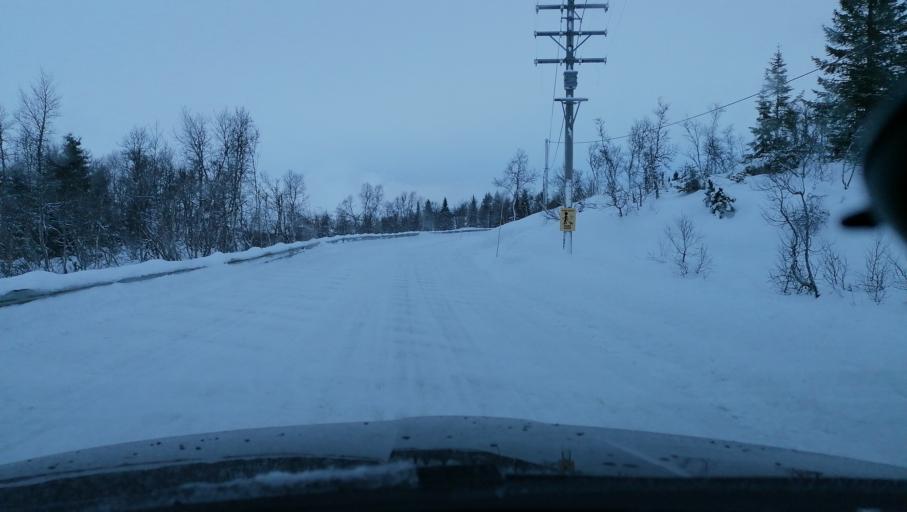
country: NO
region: Aust-Agder
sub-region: Bykle
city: Hovden
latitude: 59.6383
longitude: 7.4536
